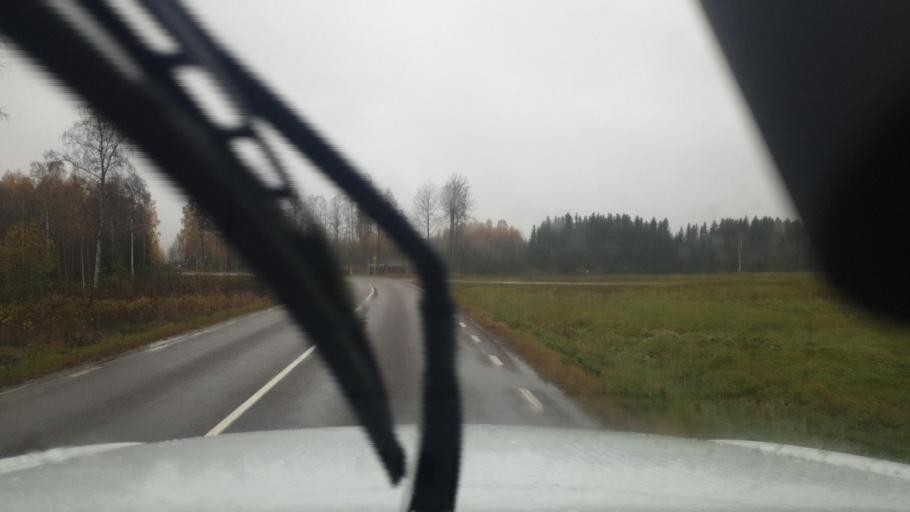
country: SE
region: Vaermland
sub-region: Sunne Kommun
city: Sunne
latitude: 59.7979
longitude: 13.0657
